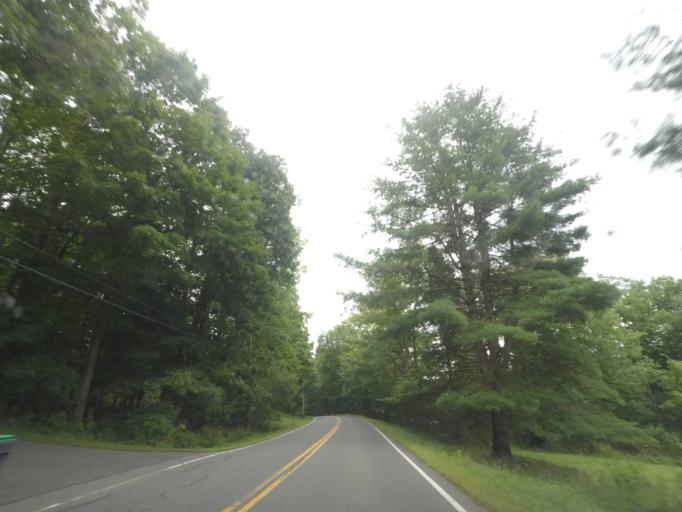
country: US
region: New York
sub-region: Rensselaer County
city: Nassau
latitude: 42.4717
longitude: -73.5886
